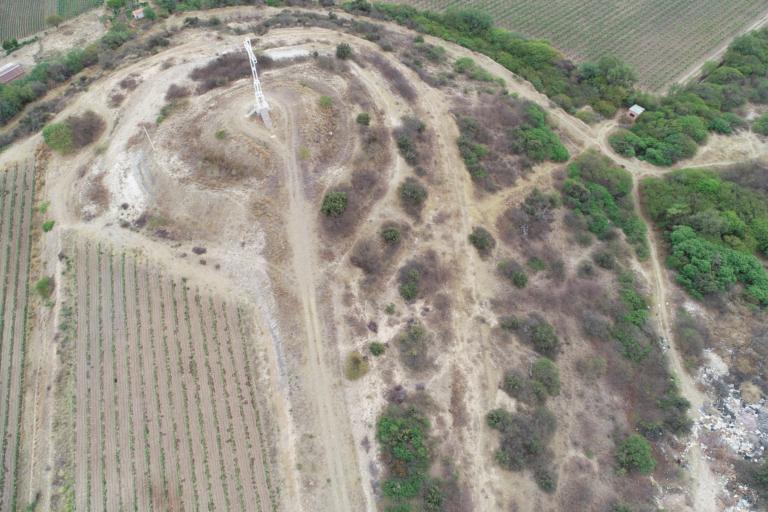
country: BO
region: Tarija
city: Tarija
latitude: -21.5948
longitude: -64.6144
